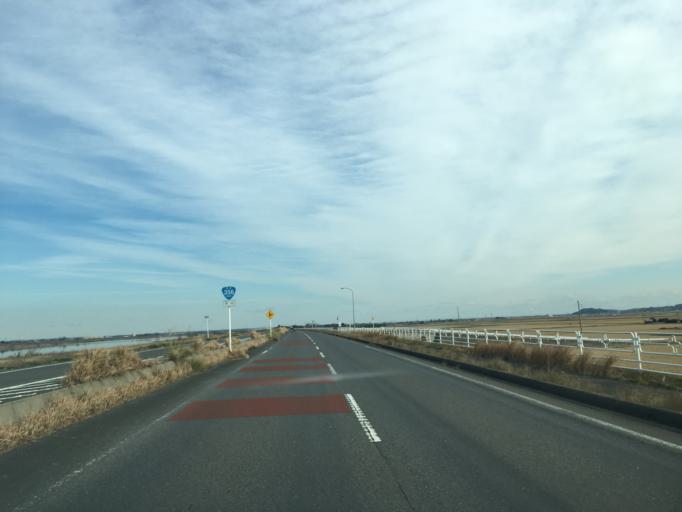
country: JP
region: Chiba
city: Katori-shi
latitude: 35.9054
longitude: 140.4260
